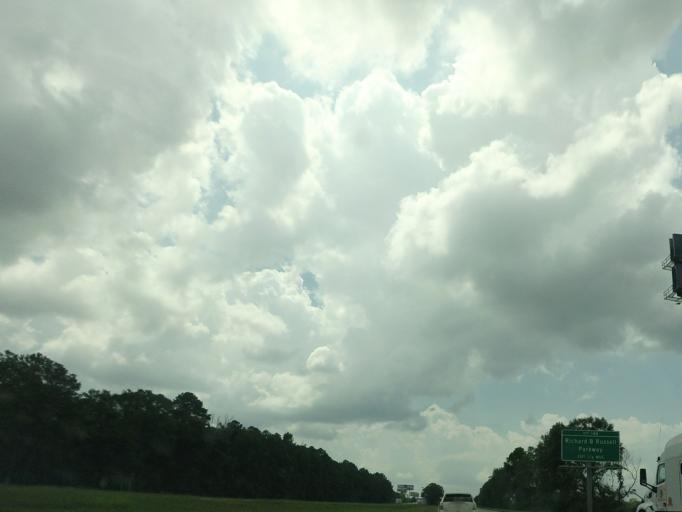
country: US
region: Georgia
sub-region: Peach County
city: Byron
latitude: 32.6009
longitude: -83.7429
